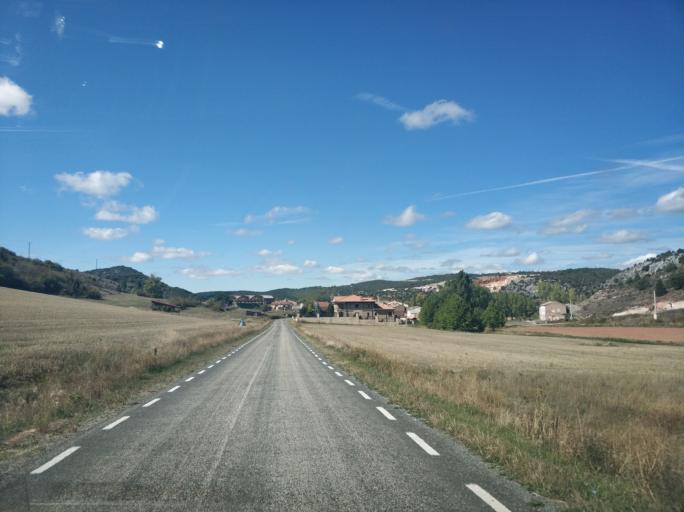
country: ES
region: Castille and Leon
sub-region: Provincia de Soria
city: Espejon
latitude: 41.8291
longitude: -3.2540
